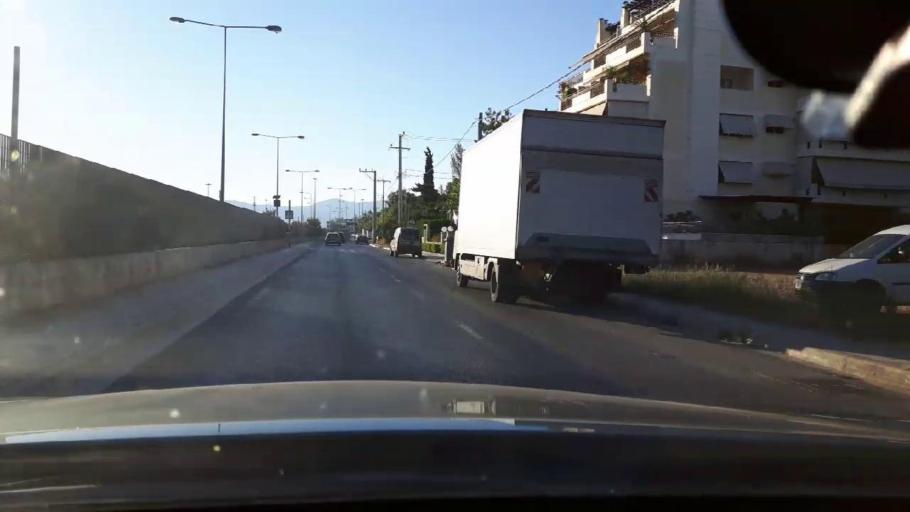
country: GR
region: Attica
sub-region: Nomarchia Athinas
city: Vrilissia
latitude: 38.0312
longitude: 23.8251
